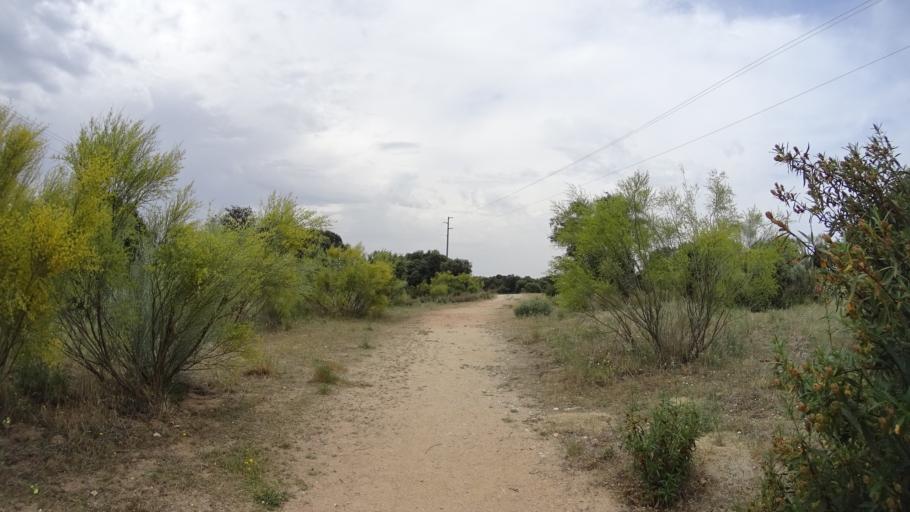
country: ES
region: Madrid
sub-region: Provincia de Madrid
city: Colmenarejo
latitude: 40.5676
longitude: -4.0333
